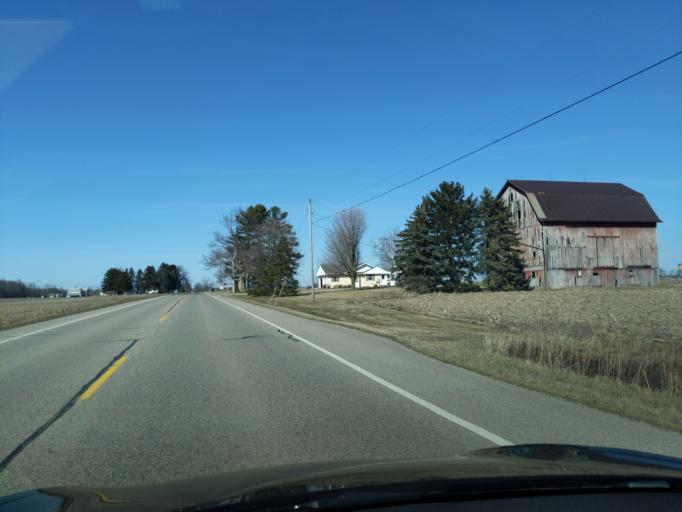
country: US
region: Michigan
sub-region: Ionia County
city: Lake Odessa
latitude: 42.8230
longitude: -85.1337
